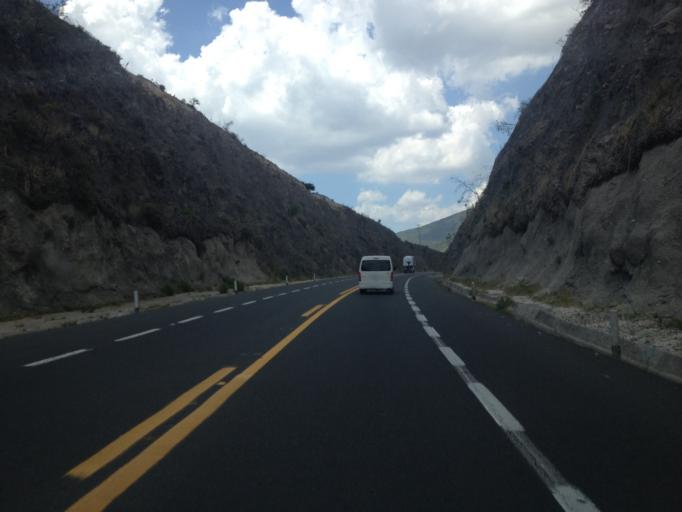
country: MX
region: Oaxaca
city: San Gabriel Casa Blanca
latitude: 17.9752
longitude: -97.3574
